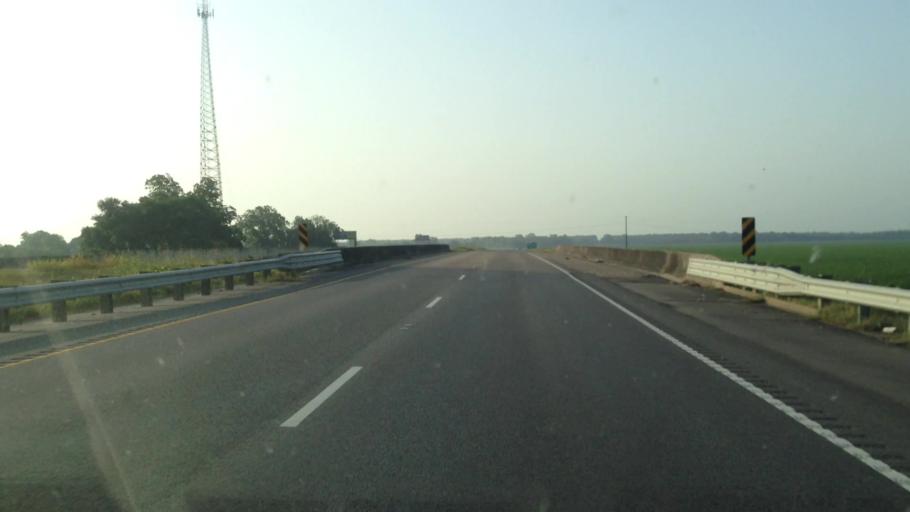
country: US
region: Louisiana
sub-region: Rapides Parish
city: Boyce
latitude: 31.3928
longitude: -92.6935
